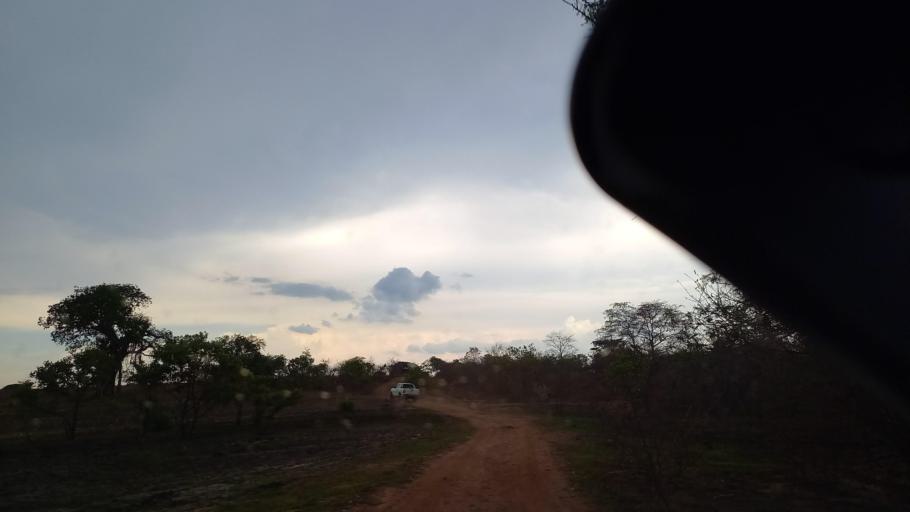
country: ZM
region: Lusaka
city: Kafue
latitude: -15.9914
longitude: 28.2718
